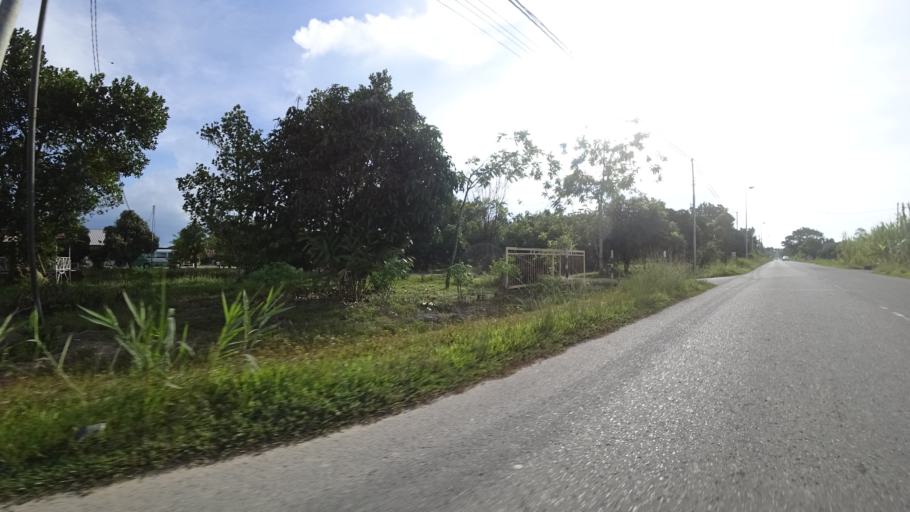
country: BN
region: Brunei and Muara
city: Bandar Seri Begawan
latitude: 4.8436
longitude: 114.8490
